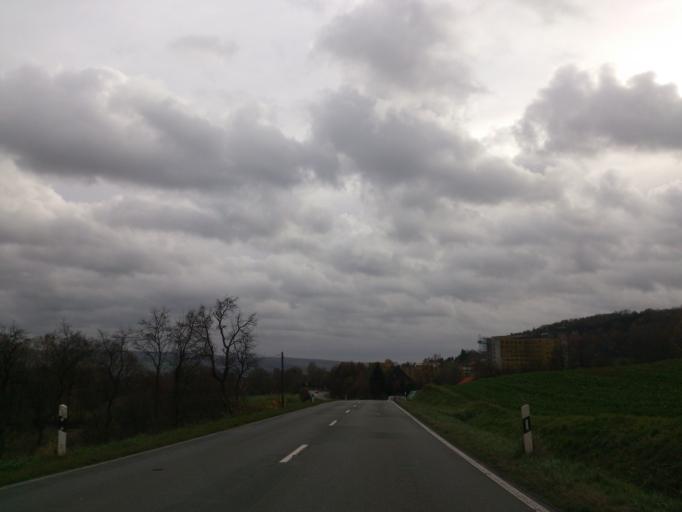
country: DE
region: North Rhine-Westphalia
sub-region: Regierungsbezirk Detmold
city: Hoexter
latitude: 51.7900
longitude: 9.3643
